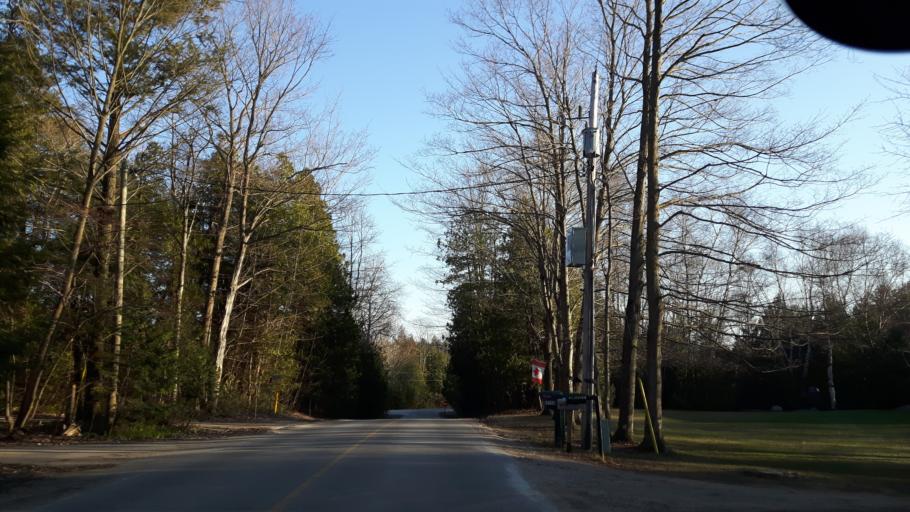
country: CA
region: Ontario
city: Bluewater
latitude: 43.5806
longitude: -81.6849
